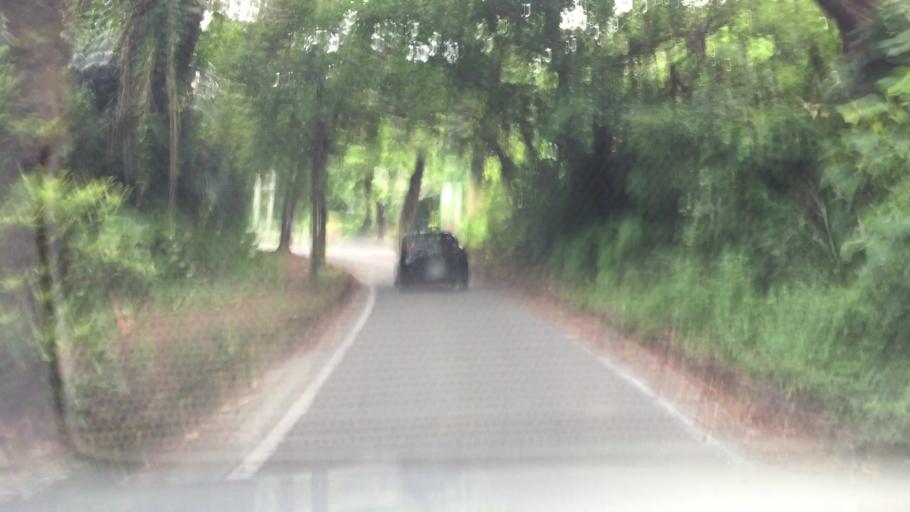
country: JP
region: Okinawa
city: Ishigaki
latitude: 24.4502
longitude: 124.1350
